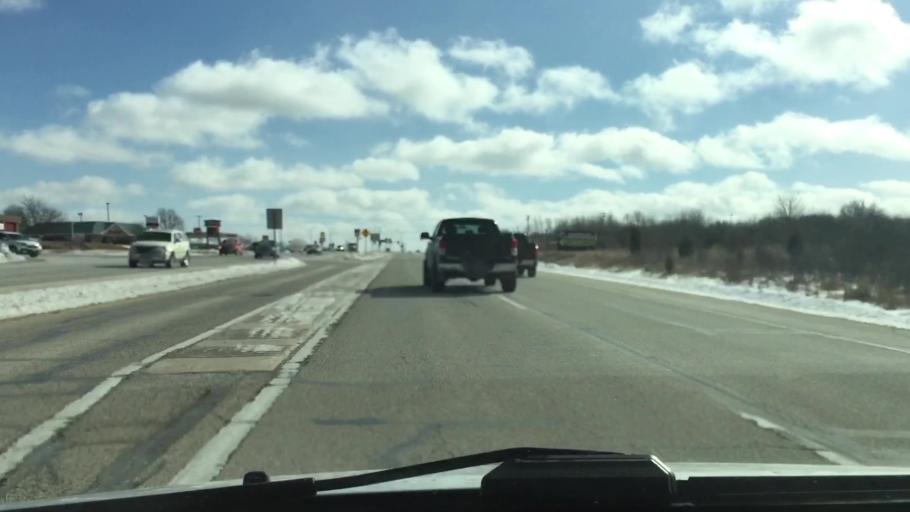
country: US
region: Wisconsin
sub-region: Waukesha County
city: Big Bend
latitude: 42.9165
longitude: -88.2222
